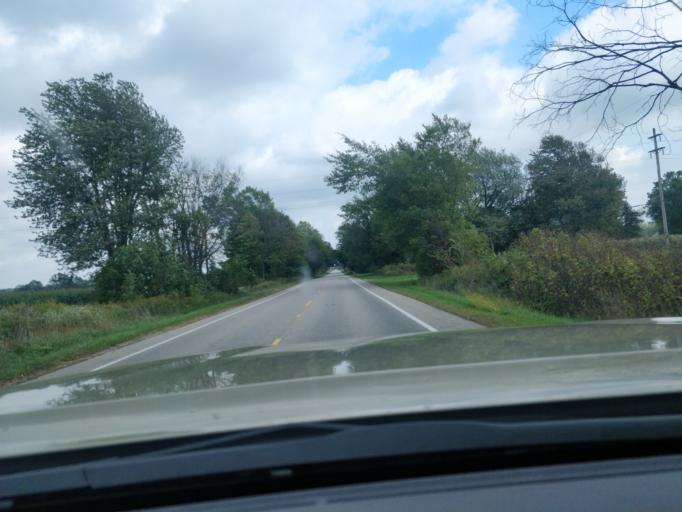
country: US
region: Michigan
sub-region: Kent County
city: Lowell
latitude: 42.8858
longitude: -85.3373
